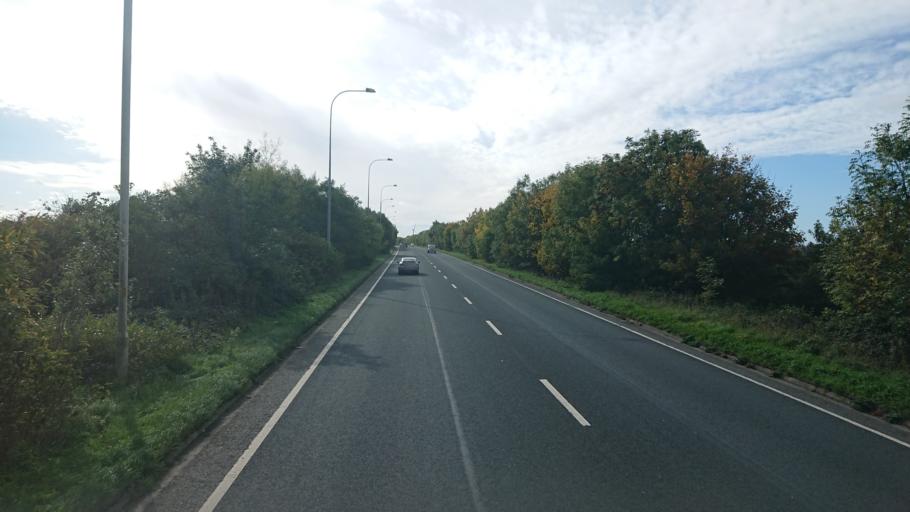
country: GB
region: England
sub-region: Lancashire
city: Morecambe
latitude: 54.0517
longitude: -2.8440
